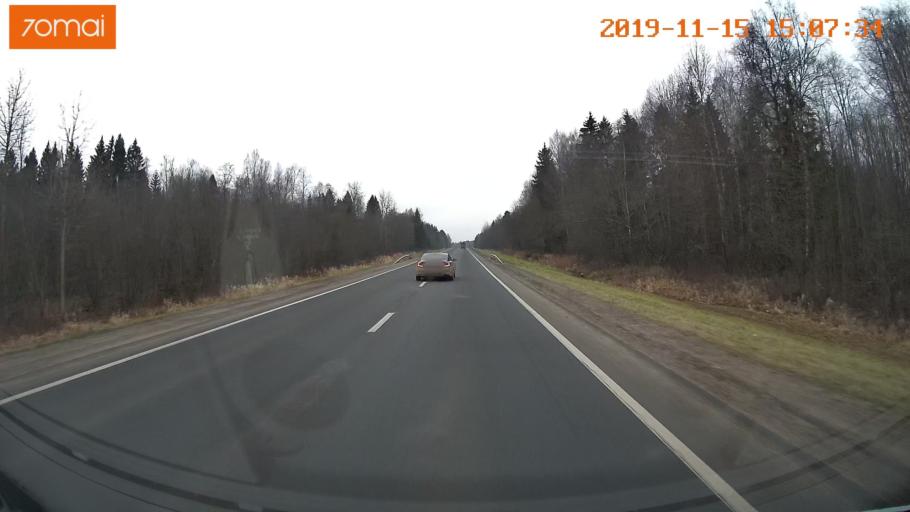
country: RU
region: Jaroslavl
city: Prechistoye
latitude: 58.3820
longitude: 40.2926
